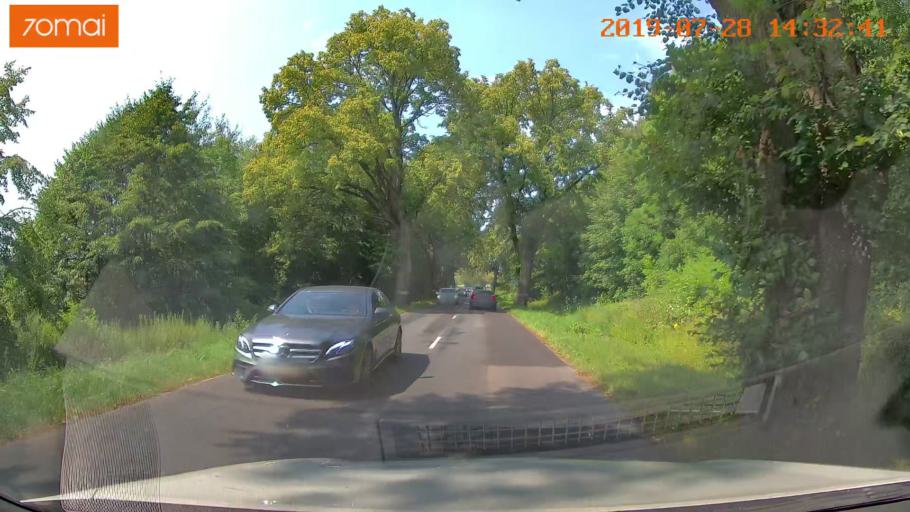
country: RU
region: Kaliningrad
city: Primorsk
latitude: 54.8144
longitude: 20.0390
